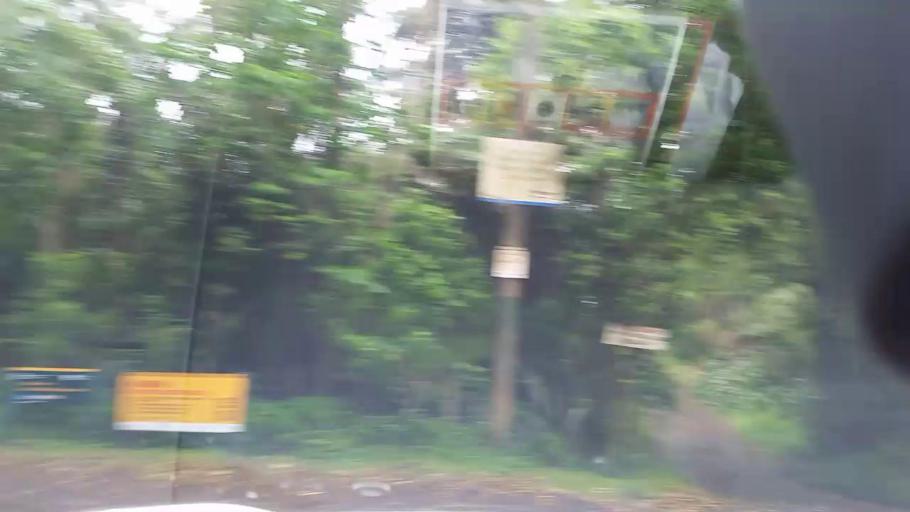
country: NZ
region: Auckland
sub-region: Auckland
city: Muriwai Beach
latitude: -36.8468
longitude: 174.4741
